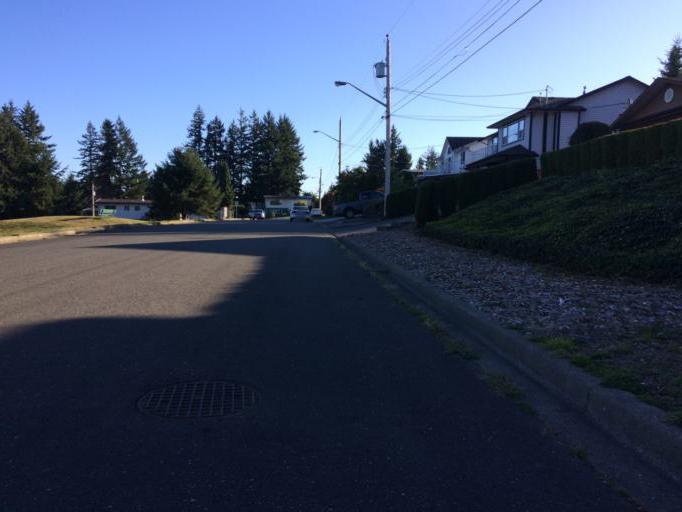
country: CA
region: British Columbia
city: Campbell River
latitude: 49.9865
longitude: -125.2309
